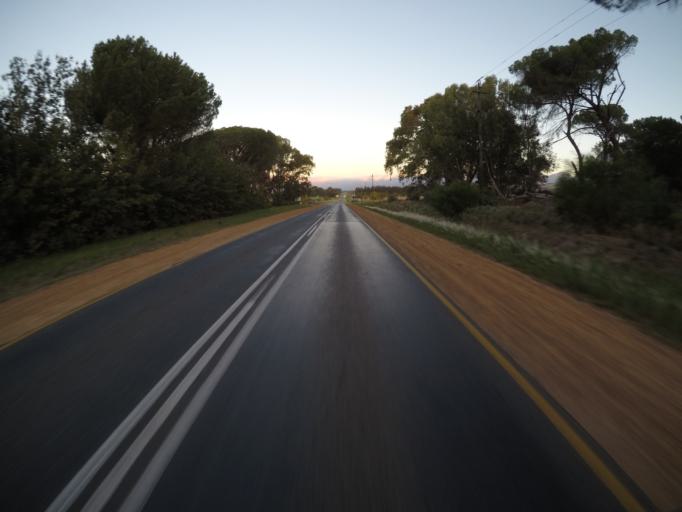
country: ZA
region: Western Cape
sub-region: Cape Winelands District Municipality
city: Paarl
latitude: -33.8131
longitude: 18.9122
